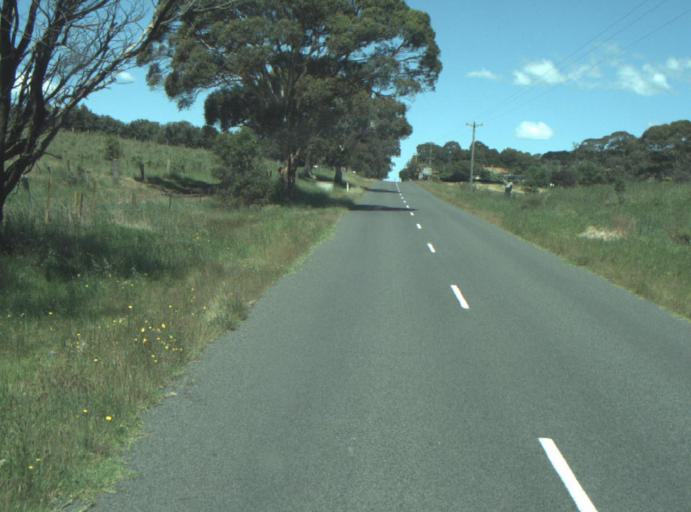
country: AU
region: Victoria
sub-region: Greater Geelong
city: Lara
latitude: -37.8773
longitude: 144.2675
